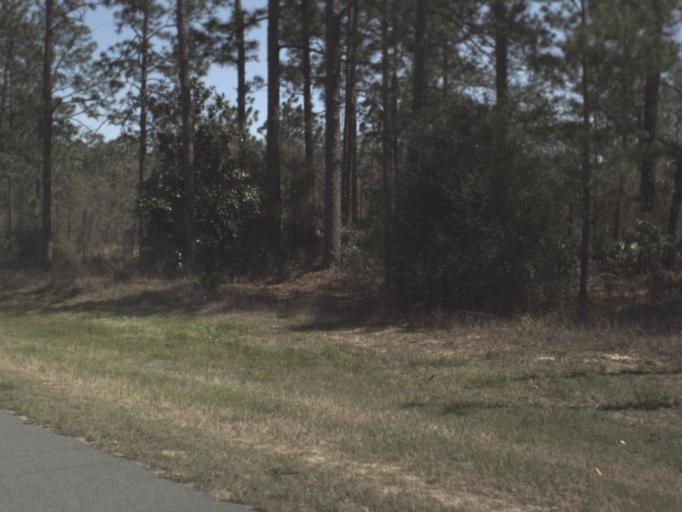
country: US
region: Florida
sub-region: Bay County
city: Youngstown
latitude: 30.4366
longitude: -85.3497
